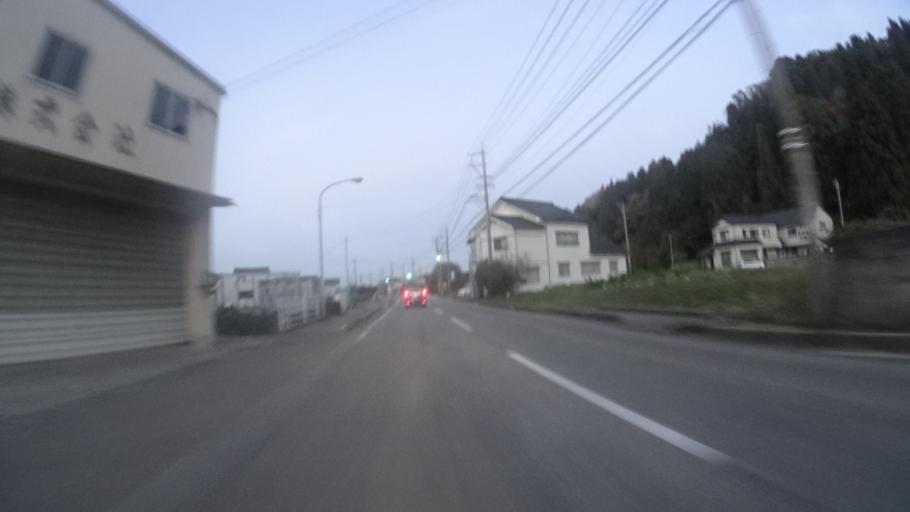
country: JP
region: Ishikawa
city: Nanao
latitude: 37.3788
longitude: 136.8843
